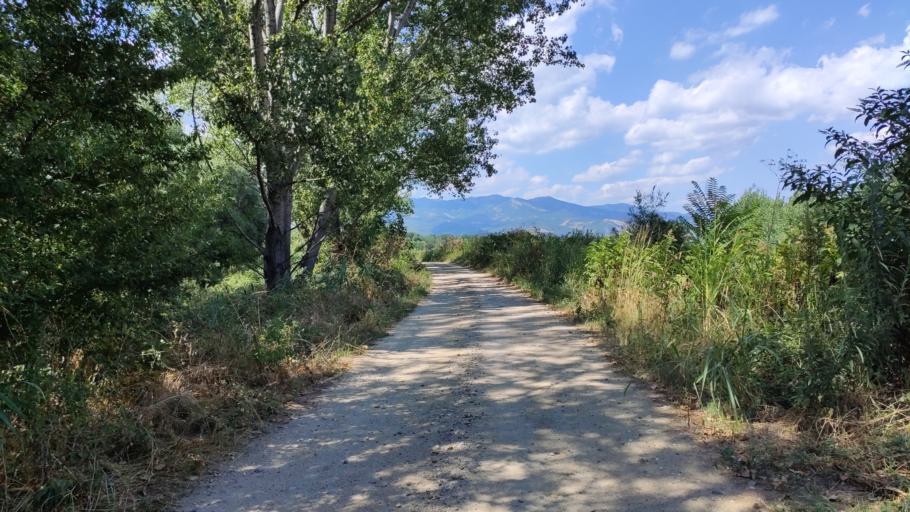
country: GR
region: East Macedonia and Thrace
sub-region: Nomos Rodopis
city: Komotini
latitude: 41.1117
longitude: 25.3709
